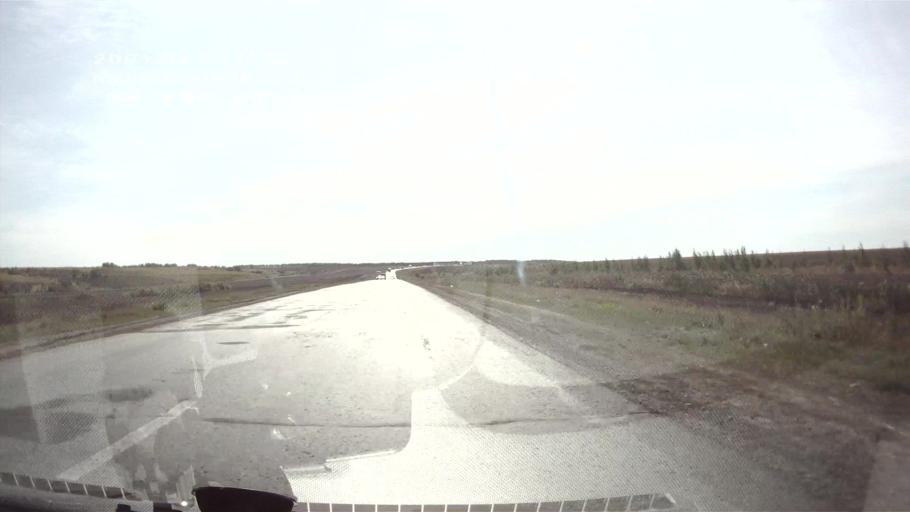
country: RU
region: Samara
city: Varlamovo
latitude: 53.0151
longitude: 48.3326
